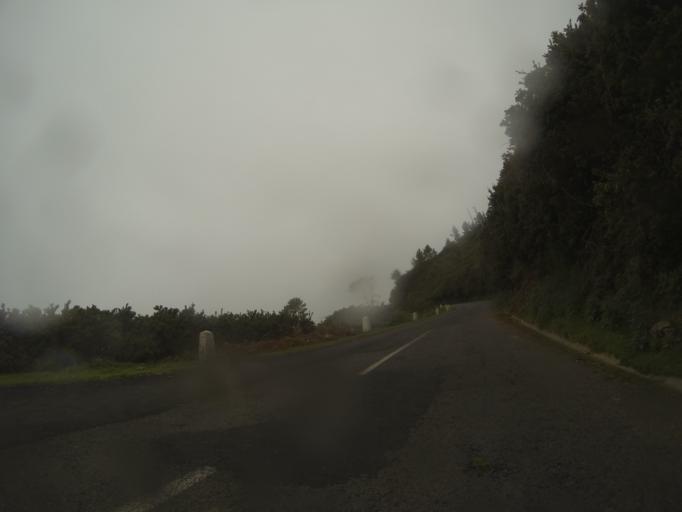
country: PT
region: Madeira
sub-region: Calheta
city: Estreito da Calheta
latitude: 32.7785
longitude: -17.1922
